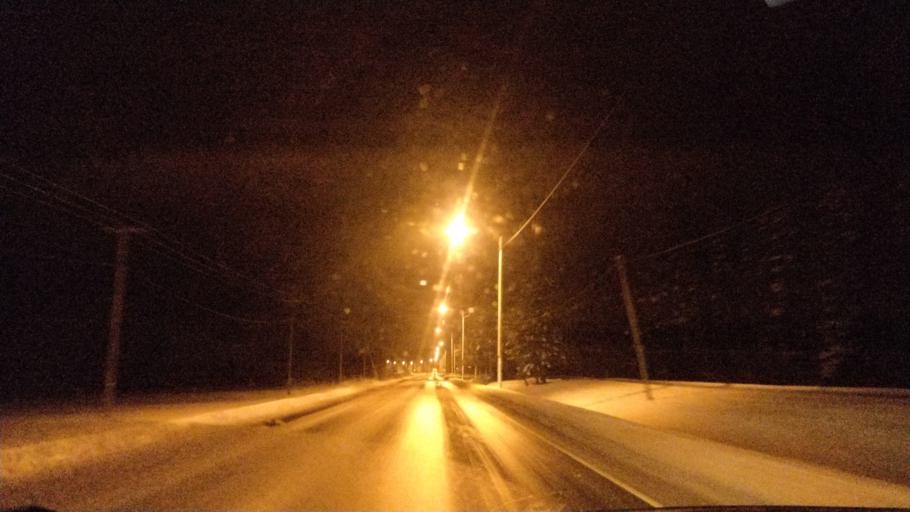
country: FI
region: Lapland
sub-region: Rovaniemi
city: Rovaniemi
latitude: 66.3064
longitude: 25.3581
